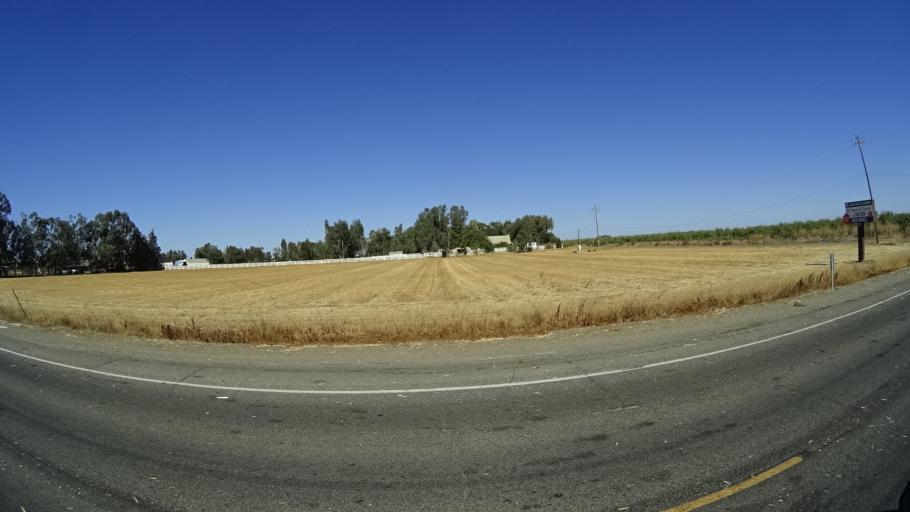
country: US
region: California
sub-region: Yolo County
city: Davis
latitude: 38.5614
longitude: -121.8503
